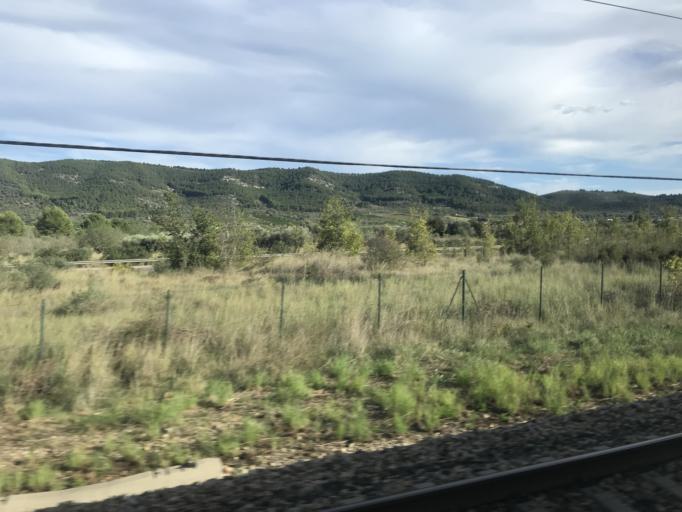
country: ES
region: Valencia
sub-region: Provincia de Castello
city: Alcala de Xivert
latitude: 40.3101
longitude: 0.2310
